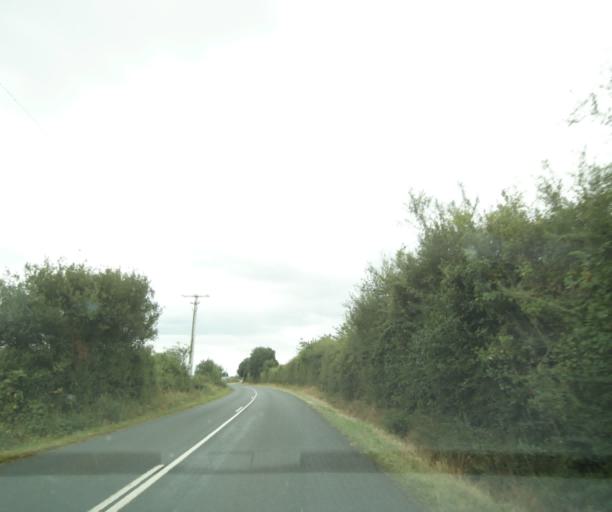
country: FR
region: Pays de la Loire
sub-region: Departement de la Sarthe
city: Sable-sur-Sarthe
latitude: 47.8176
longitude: -0.3187
